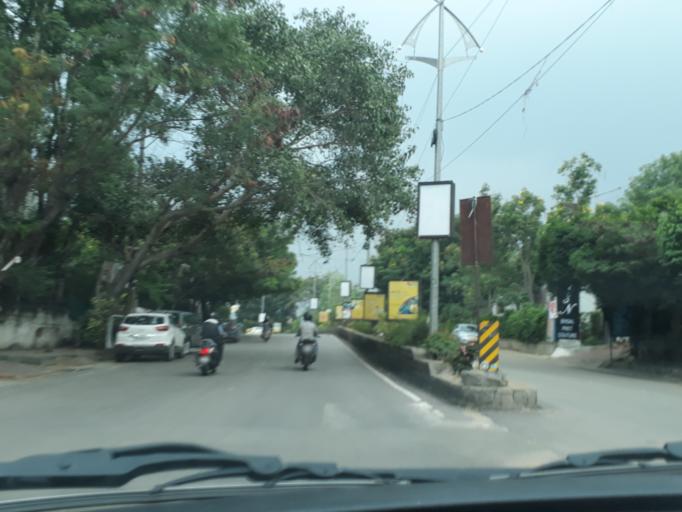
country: IN
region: Telangana
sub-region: Rangareddi
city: Kukatpalli
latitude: 17.4322
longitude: 78.4183
